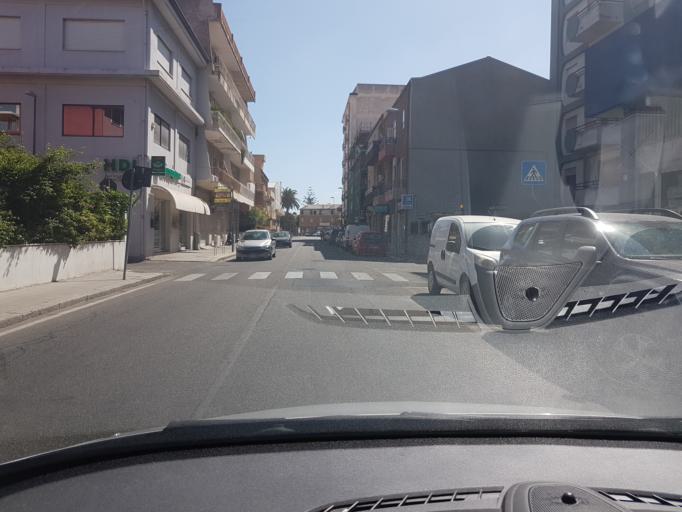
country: IT
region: Sardinia
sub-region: Provincia di Oristano
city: Oristano
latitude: 39.9086
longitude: 8.5938
